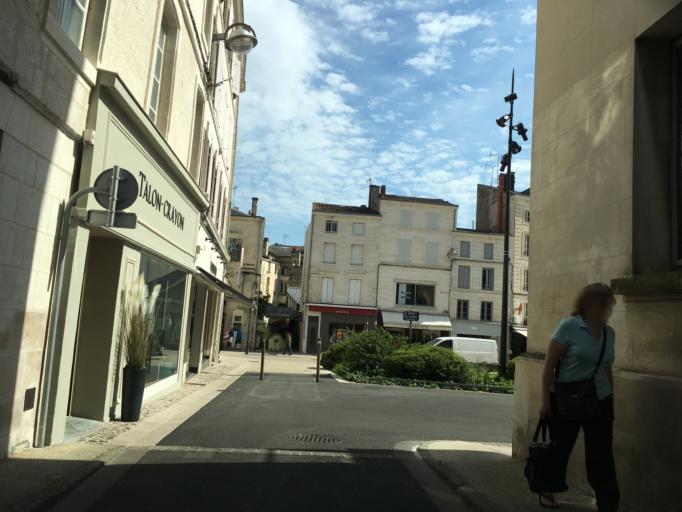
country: FR
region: Poitou-Charentes
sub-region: Departement des Deux-Sevres
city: Niort
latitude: 46.3231
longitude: -0.4615
